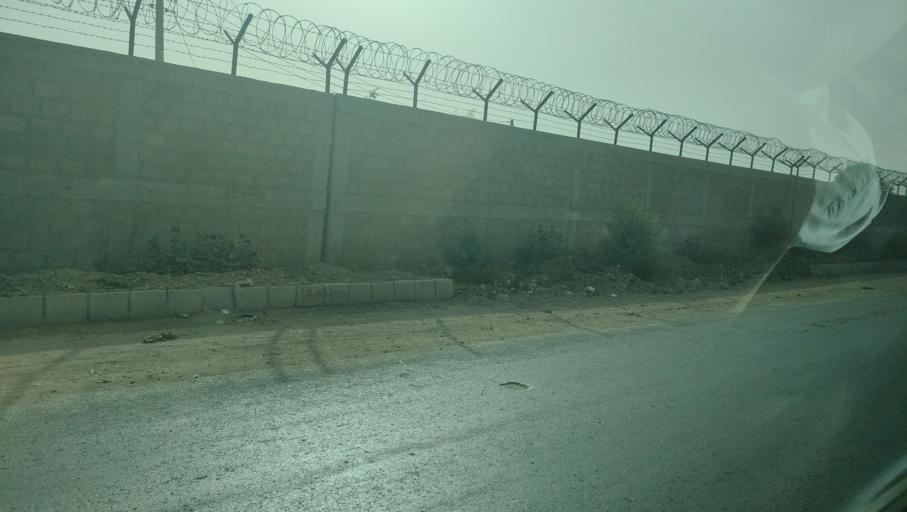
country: PK
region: Sindh
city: Malir Cantonment
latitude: 24.9187
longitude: 67.1868
